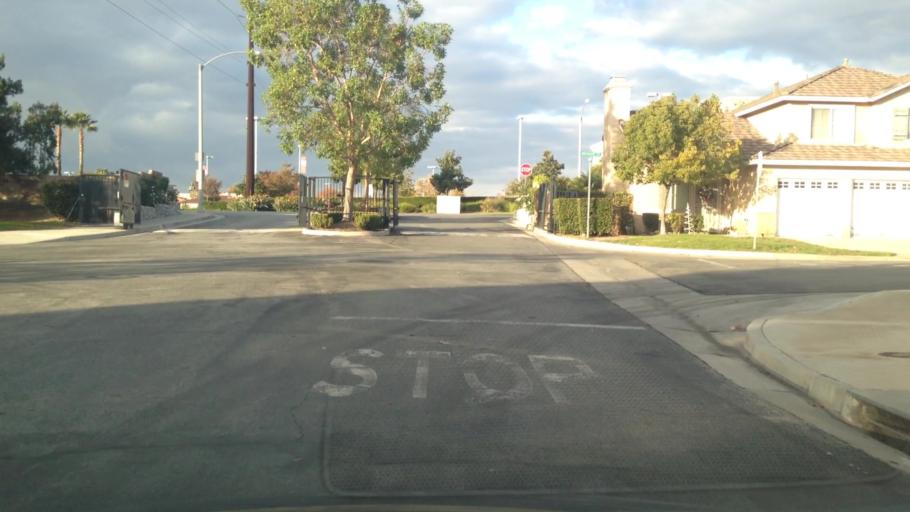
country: US
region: California
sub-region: Riverside County
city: Woodcrest
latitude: 33.9129
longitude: -117.3223
